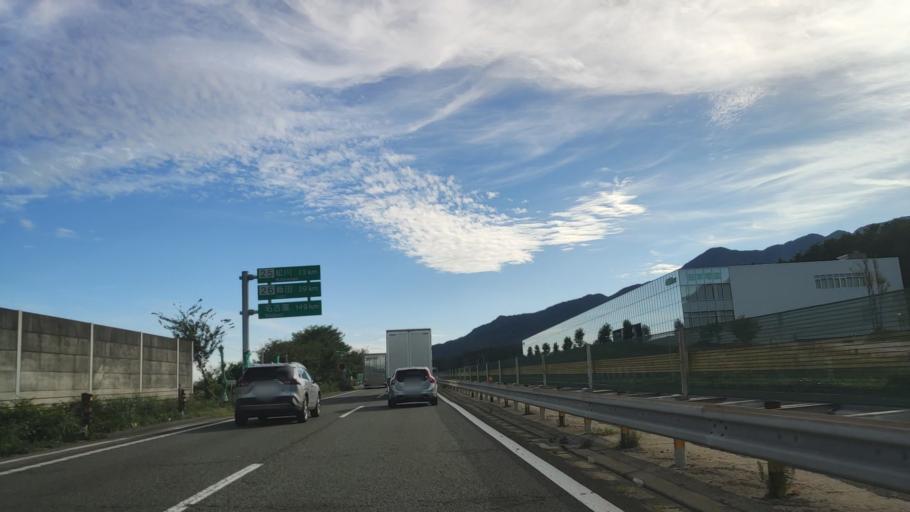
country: JP
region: Nagano
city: Ina
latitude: 35.7256
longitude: 137.9093
